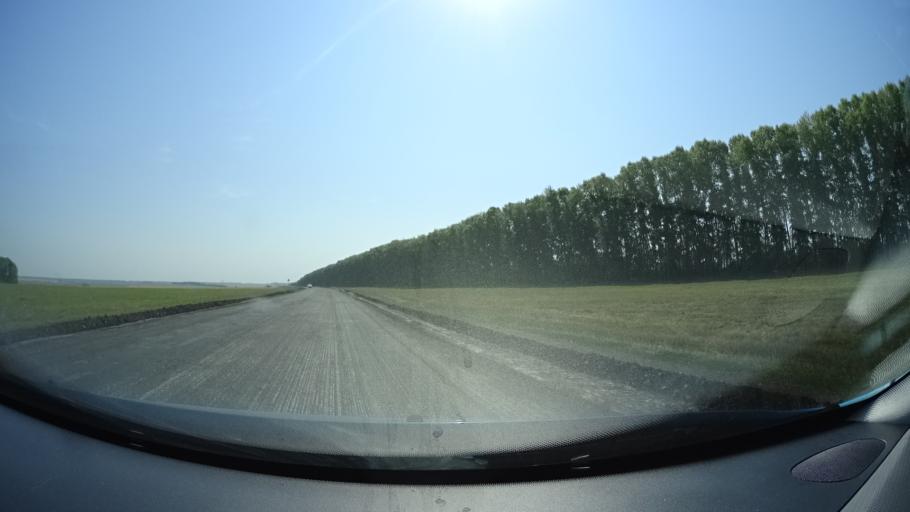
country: RU
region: Bashkortostan
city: Kabakovo
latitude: 54.4506
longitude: 55.9754
